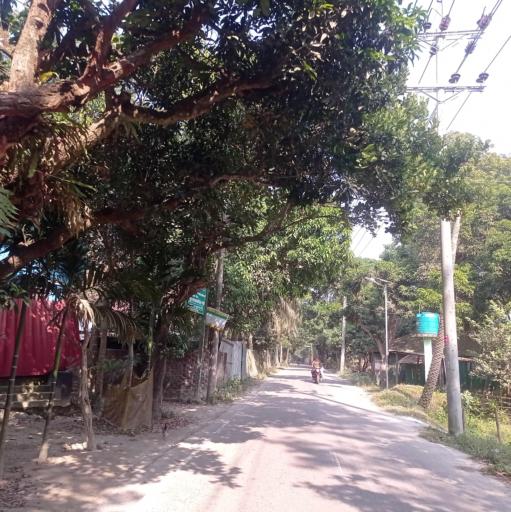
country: BD
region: Dhaka
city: Narsingdi
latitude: 24.0423
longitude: 90.6787
